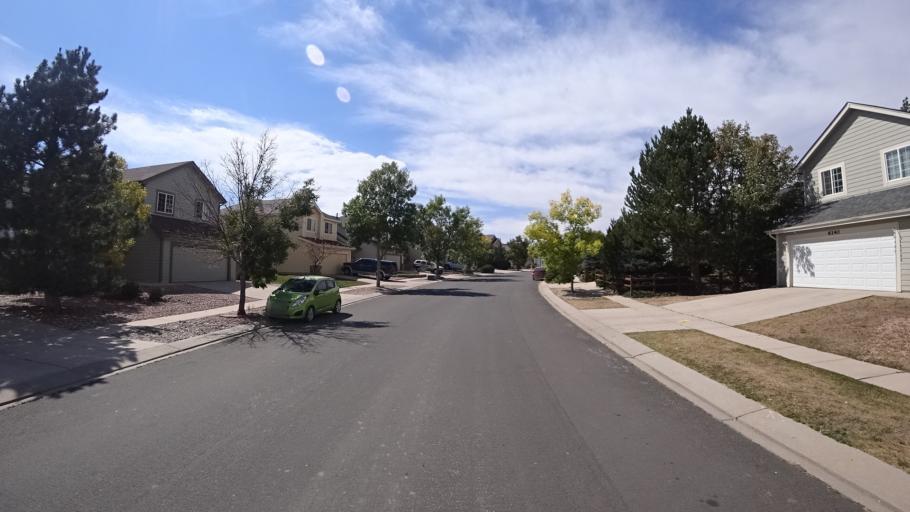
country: US
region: Colorado
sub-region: El Paso County
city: Cimarron Hills
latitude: 38.8978
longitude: -104.7130
